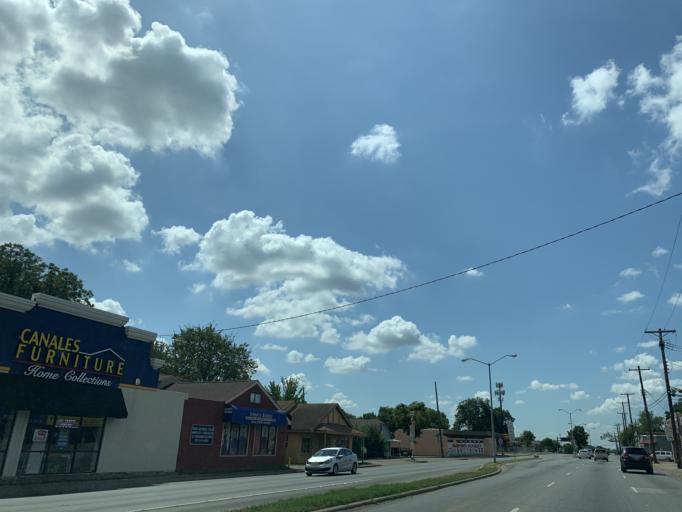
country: US
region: Texas
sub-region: Dallas County
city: Cockrell Hill
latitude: 32.7402
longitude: -96.8568
